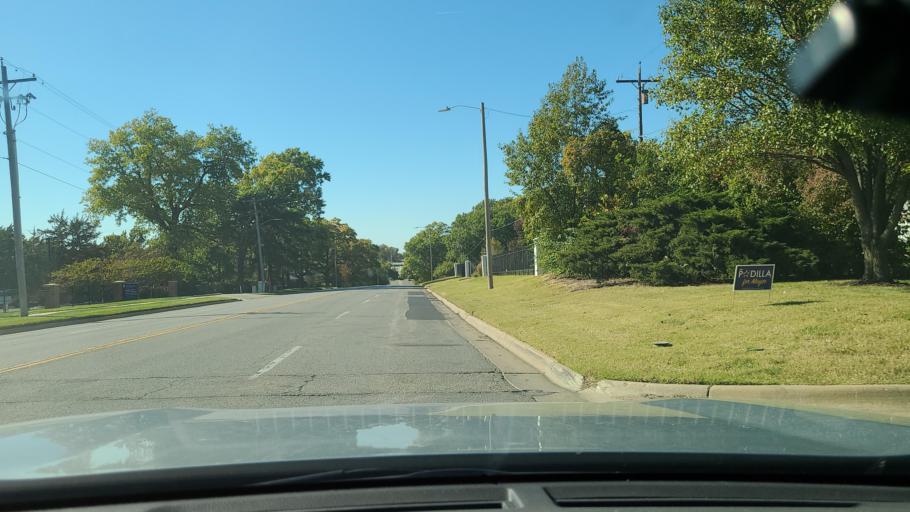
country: US
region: Kansas
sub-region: Shawnee County
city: Topeka
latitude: 39.0152
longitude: -95.6908
